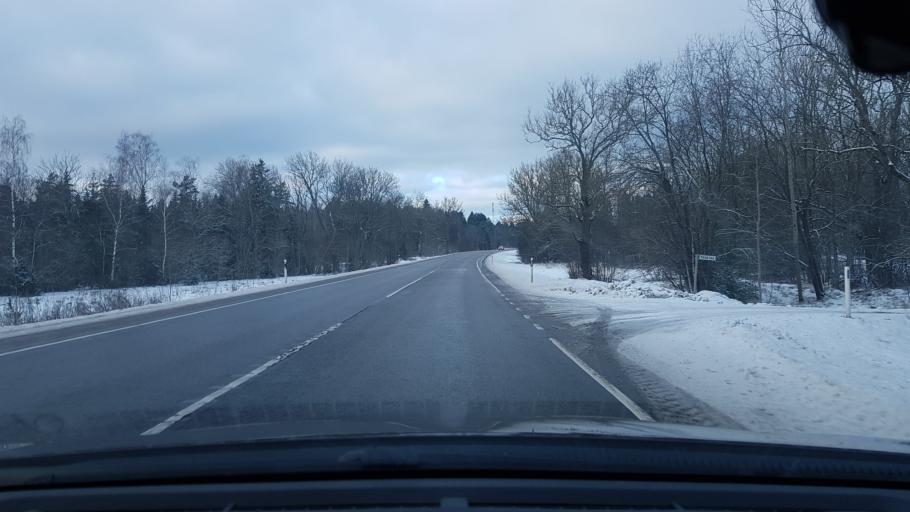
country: EE
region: Harju
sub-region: Keila linn
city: Keila
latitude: 59.3370
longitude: 24.2767
